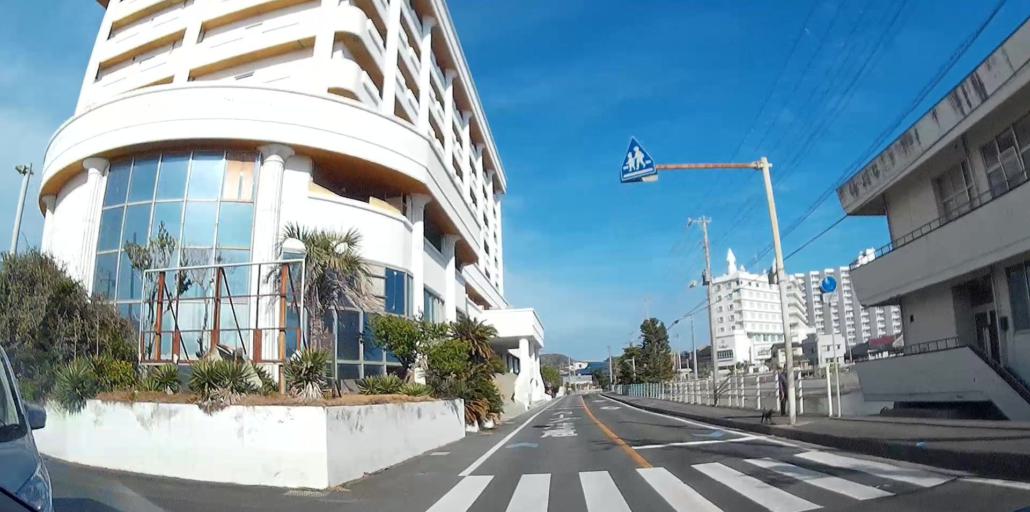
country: JP
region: Chiba
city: Tateyama
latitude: 34.9060
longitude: 139.8973
